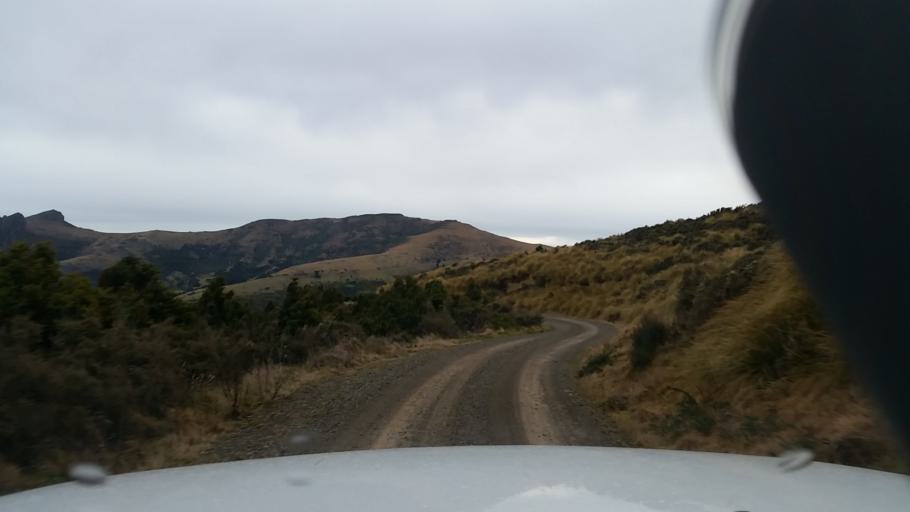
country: NZ
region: Canterbury
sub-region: Christchurch City
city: Christchurch
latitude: -43.8208
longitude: 172.8649
